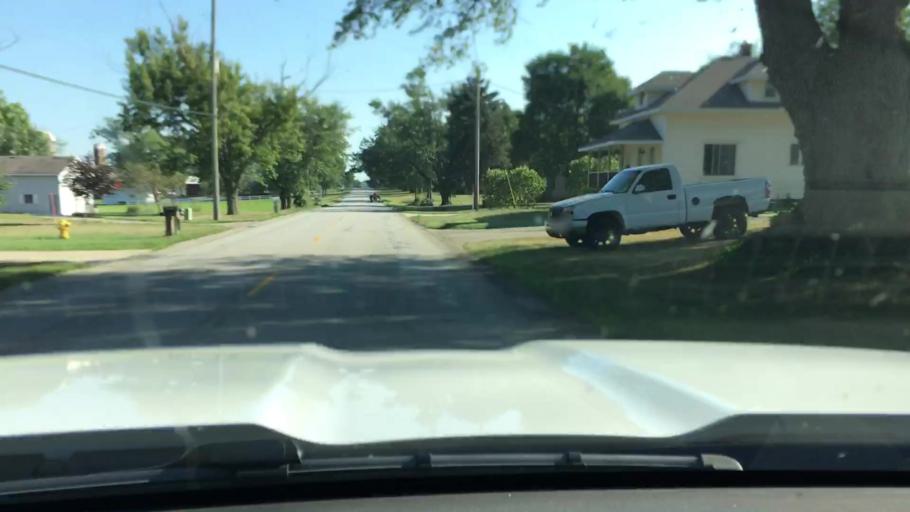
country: US
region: Michigan
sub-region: Ottawa County
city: Zeeland
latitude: 42.8477
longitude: -85.9599
